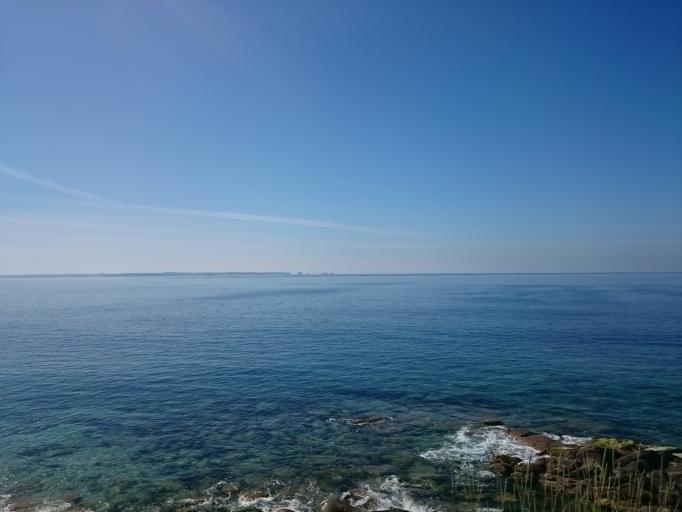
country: FR
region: Brittany
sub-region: Departement du Finistere
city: Plougonvelin
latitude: 48.3529
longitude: -4.6683
